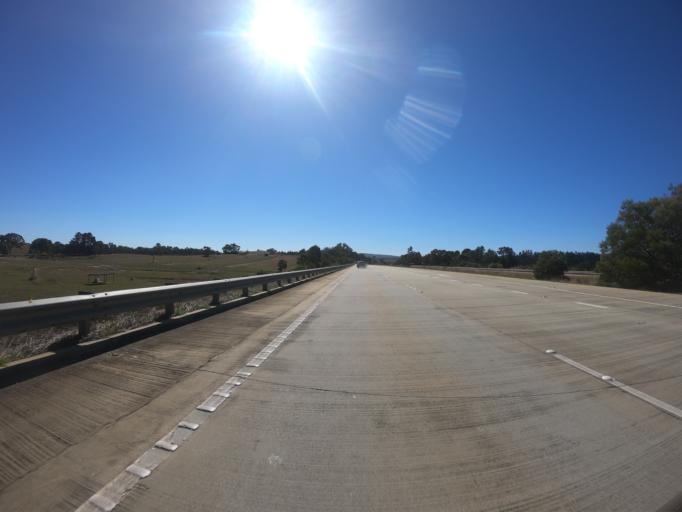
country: AU
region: New South Wales
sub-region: Yass Valley
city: Gundaroo
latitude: -35.1282
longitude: 149.3420
